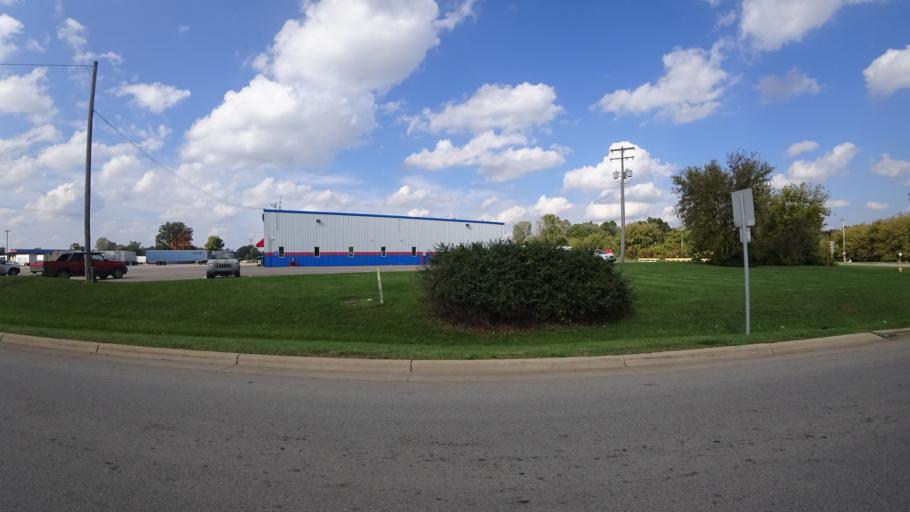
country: US
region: Michigan
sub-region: Branch County
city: Union City
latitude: 42.1064
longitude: -84.9872
